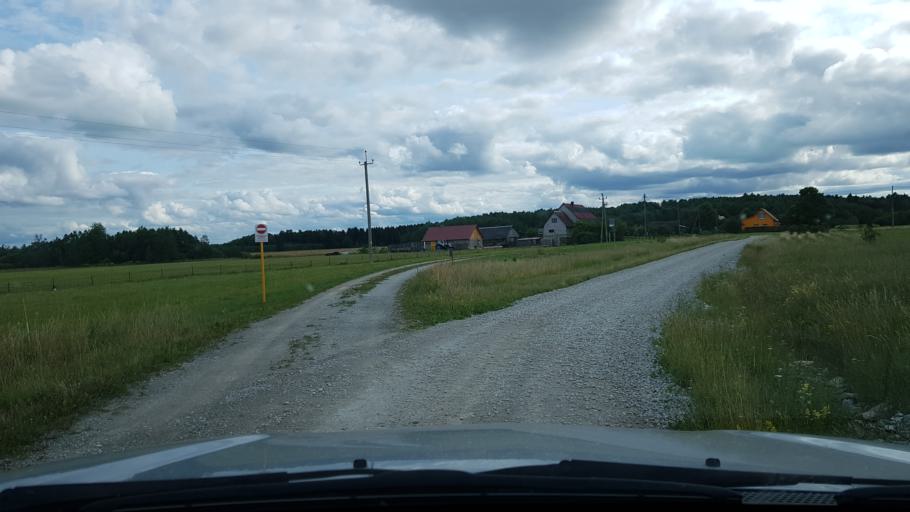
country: EE
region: Ida-Virumaa
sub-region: Narva-Joesuu linn
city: Narva-Joesuu
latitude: 59.3976
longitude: 28.0583
